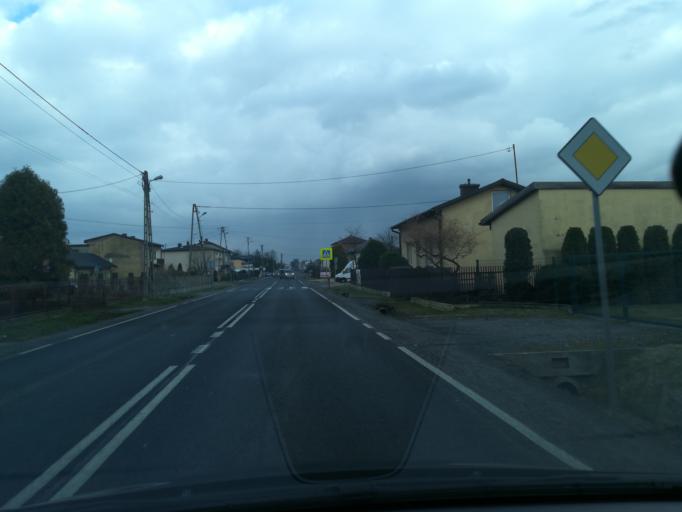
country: PL
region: Lodz Voivodeship
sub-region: Powiat radomszczanski
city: Radomsko
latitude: 51.0783
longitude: 19.3857
